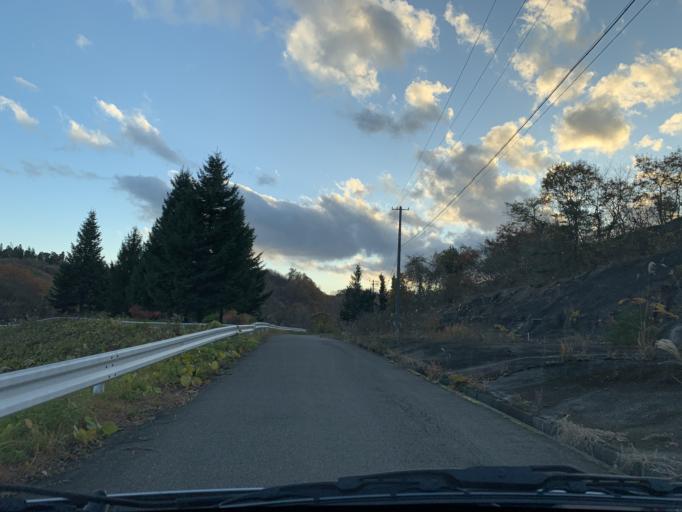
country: JP
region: Iwate
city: Ichinoseki
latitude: 39.0248
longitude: 141.0325
